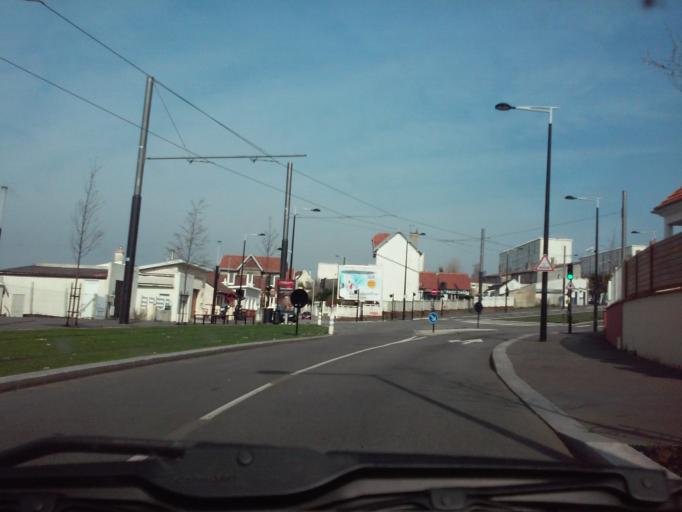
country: FR
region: Haute-Normandie
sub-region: Departement de la Seine-Maritime
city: Fontaine-la-Mallet
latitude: 49.5095
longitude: 0.1508
